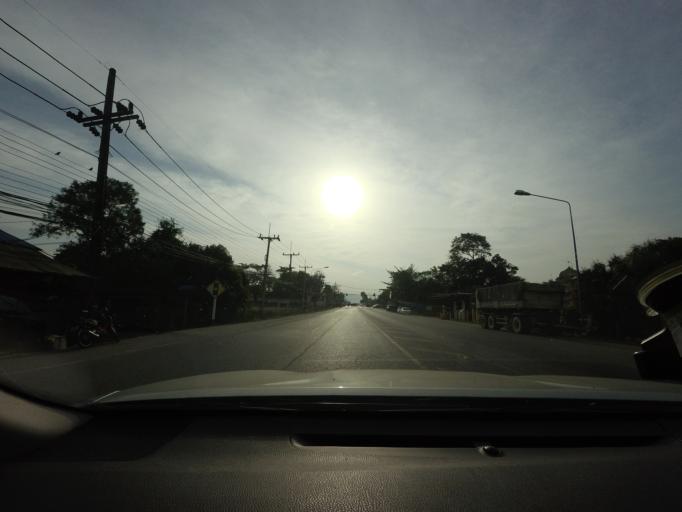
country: TH
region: Narathiwat
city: Ra-ngae
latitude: 6.2976
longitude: 101.7302
